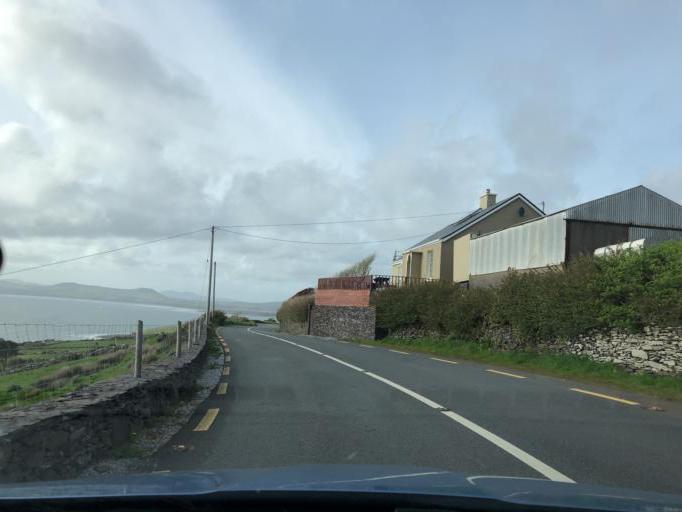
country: IE
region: Munster
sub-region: Ciarrai
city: Cahersiveen
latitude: 51.7965
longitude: -10.1665
